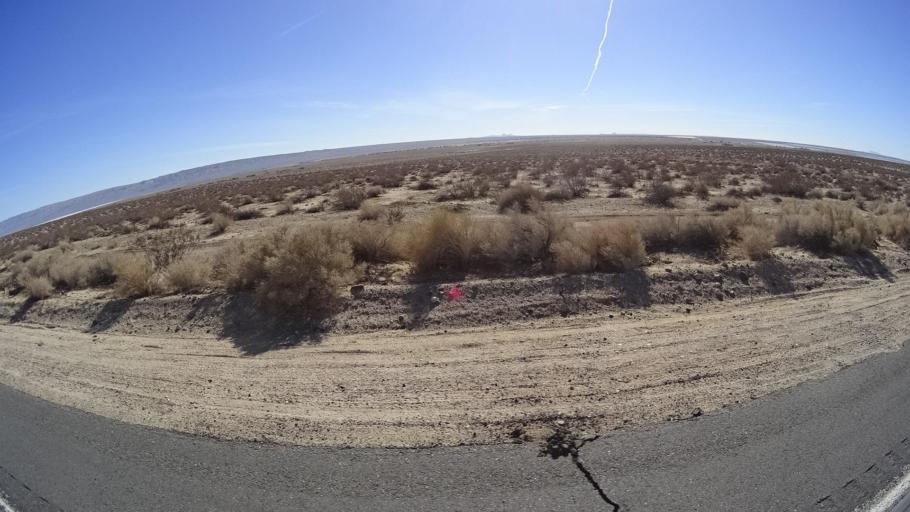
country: US
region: California
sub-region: Kern County
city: California City
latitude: 35.3144
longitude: -117.9836
